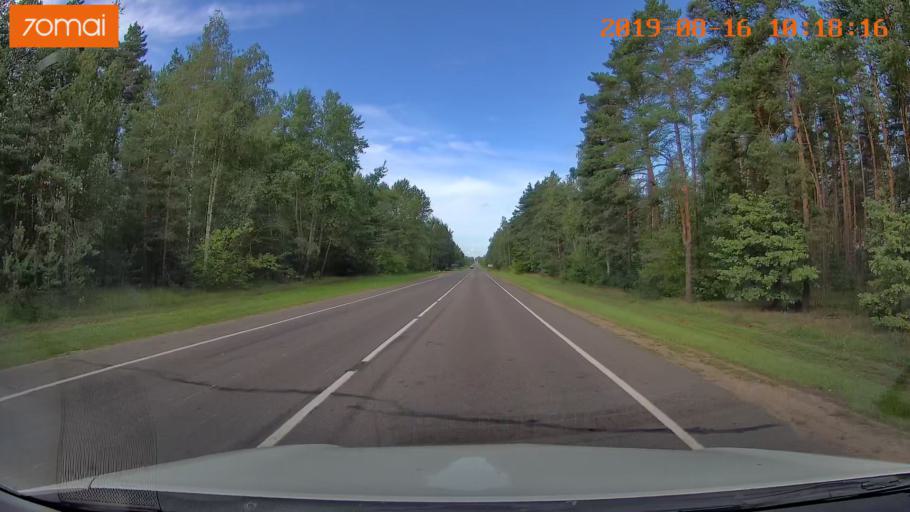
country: BY
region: Mogilev
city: Asipovichy
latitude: 53.3058
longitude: 28.6947
